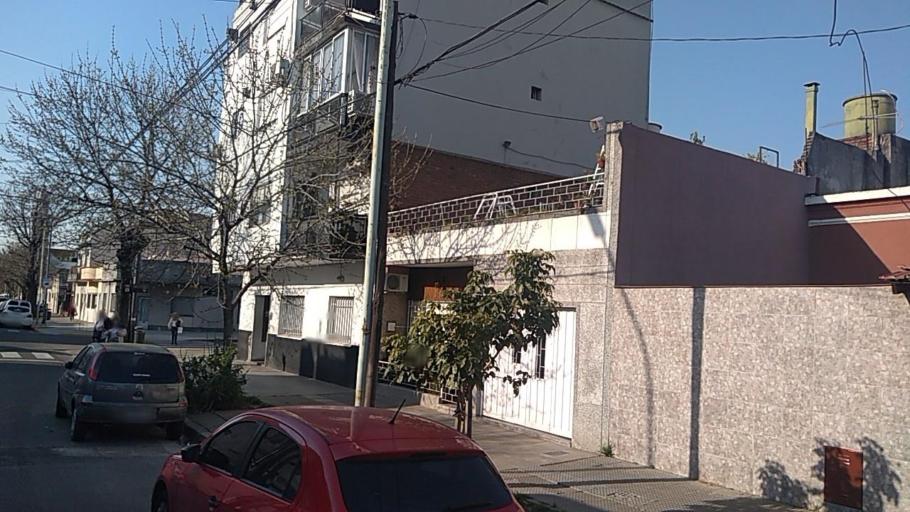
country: AR
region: Buenos Aires F.D.
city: Villa Santa Rita
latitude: -34.6265
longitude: -58.5032
